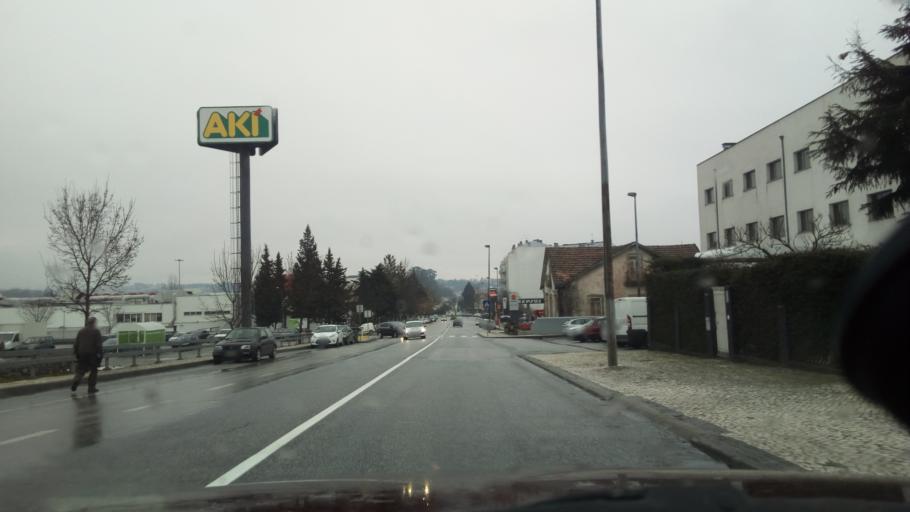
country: PT
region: Viseu
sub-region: Viseu
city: Abraveses
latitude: 40.6737
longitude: -7.9215
